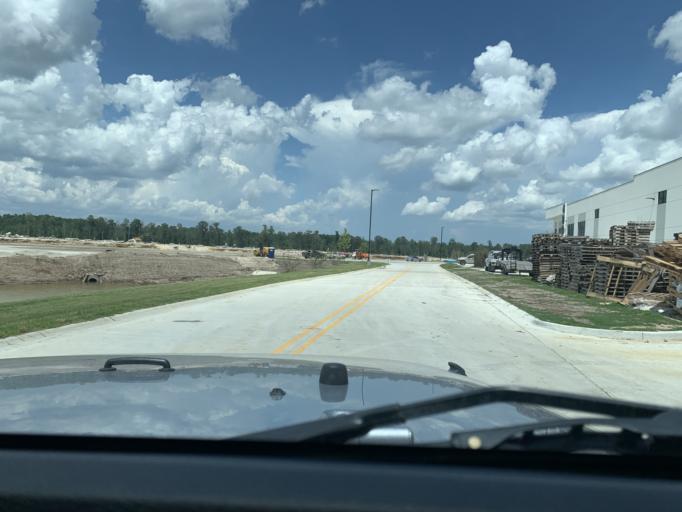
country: US
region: Georgia
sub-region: Chatham County
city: Bloomingdale
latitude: 32.1168
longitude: -81.2826
